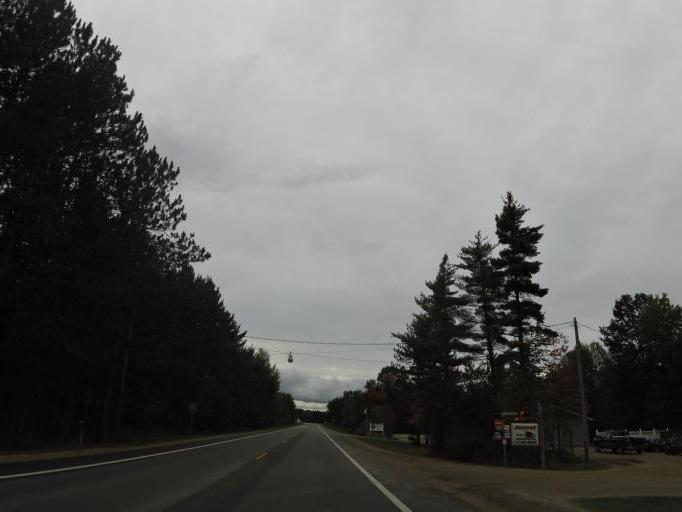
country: US
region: Michigan
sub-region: Roscommon County
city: Roscommon
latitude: 44.5064
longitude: -84.6057
